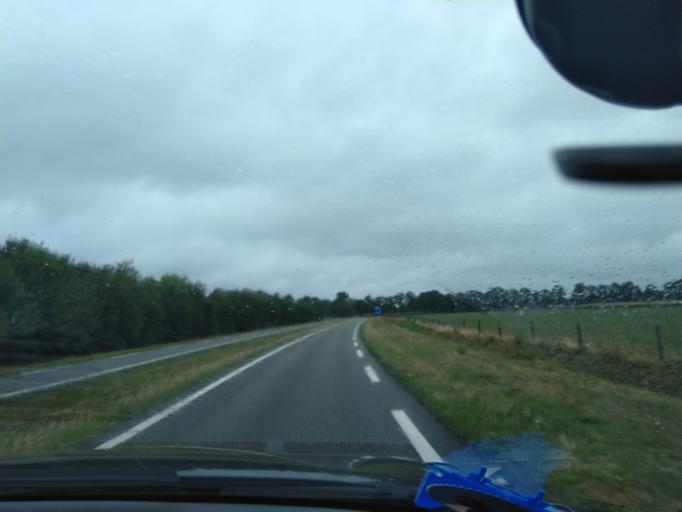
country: DE
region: Lower Saxony
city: Nordhorn
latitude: 52.3783
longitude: 7.0248
